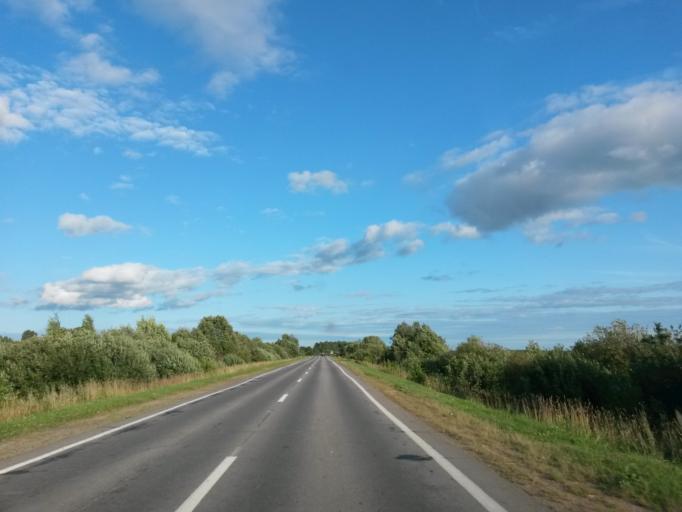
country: RU
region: Jaroslavl
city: Konstantinovskiy
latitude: 57.8507
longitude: 39.6281
